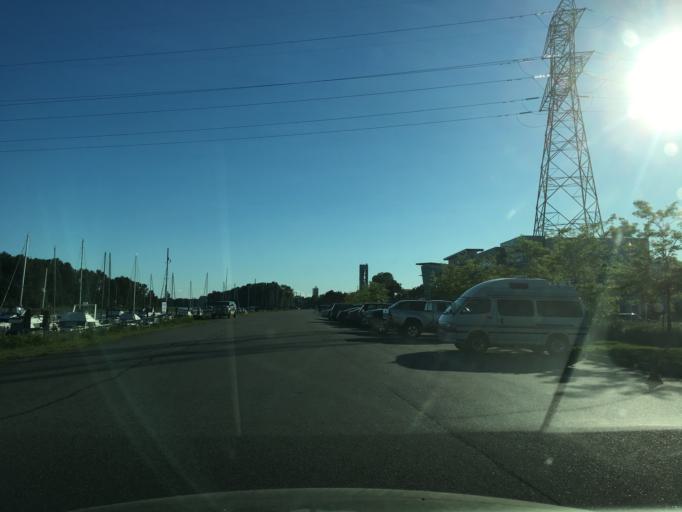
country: CA
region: British Columbia
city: Delta
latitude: 49.1645
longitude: -122.9863
